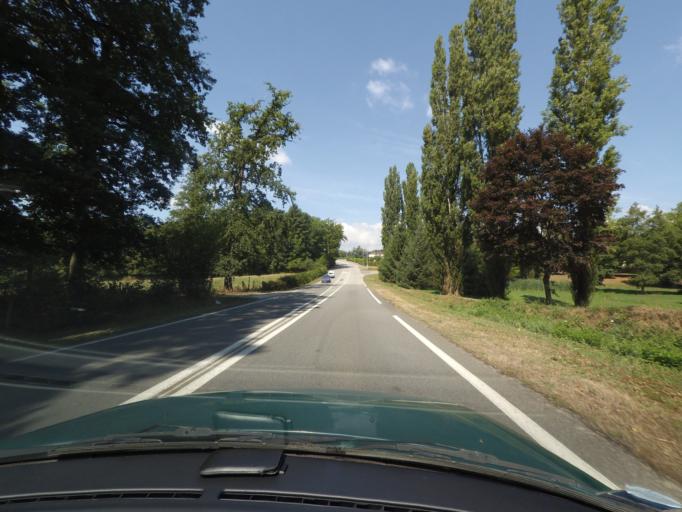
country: FR
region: Limousin
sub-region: Departement de la Haute-Vienne
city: Feytiat
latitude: 45.8122
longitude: 1.3397
